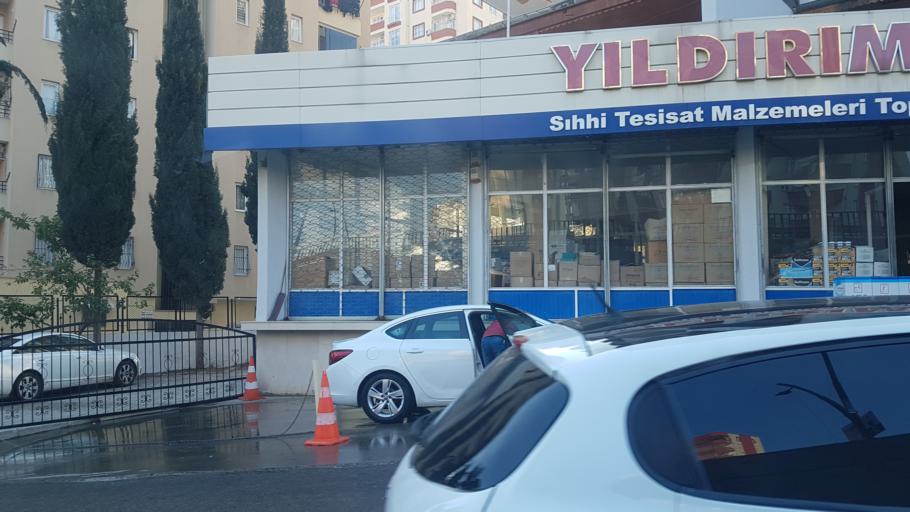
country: TR
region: Adana
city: Seyhan
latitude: 37.0314
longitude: 35.2904
